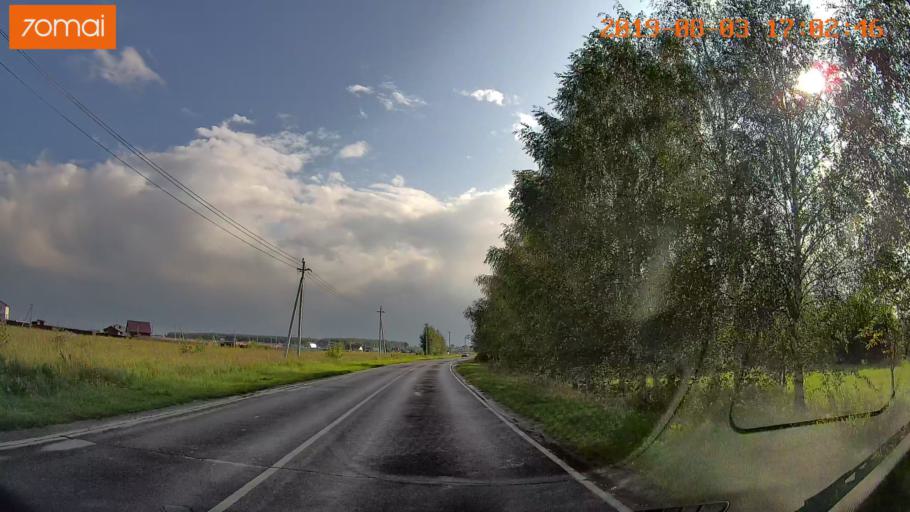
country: RU
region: Moskovskaya
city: Troitskoye
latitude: 55.3438
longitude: 38.5818
